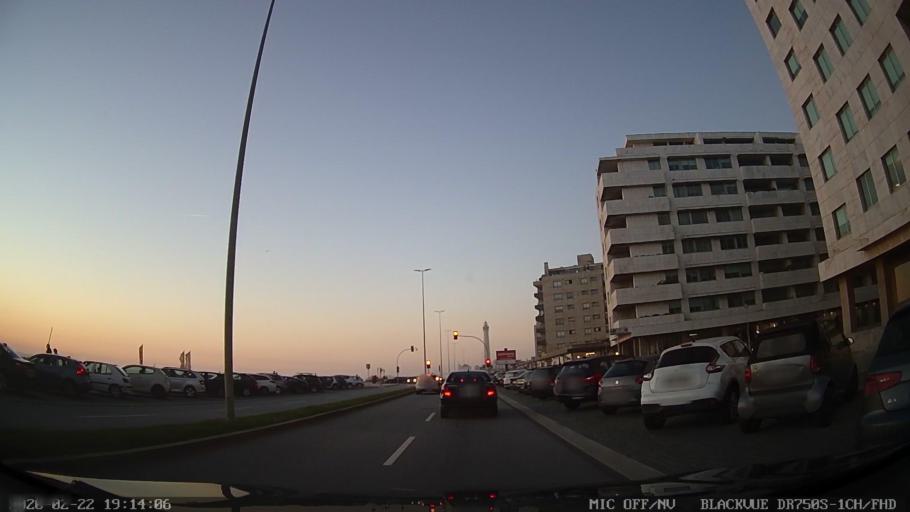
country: PT
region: Porto
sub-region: Matosinhos
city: Leca da Palmeira
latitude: 41.1975
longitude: -8.7098
